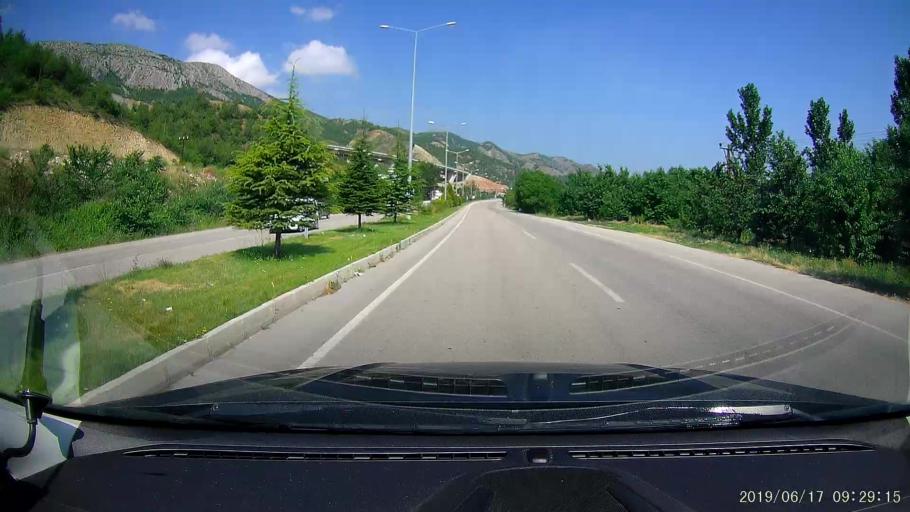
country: TR
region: Amasya
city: Amasya
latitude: 40.6953
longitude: 35.8143
